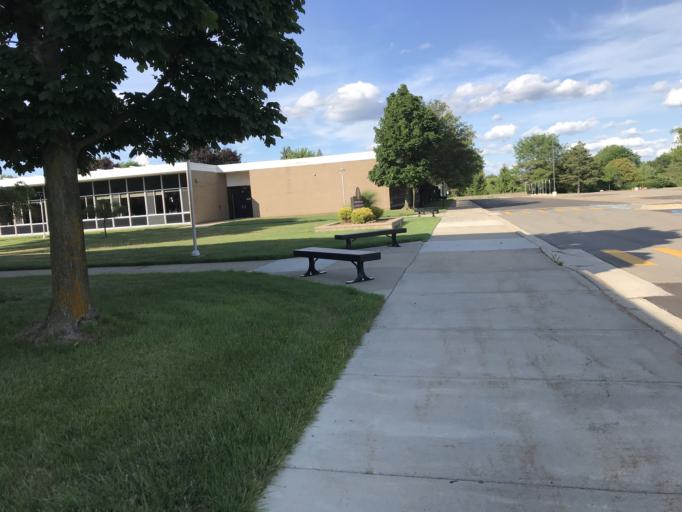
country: US
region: Michigan
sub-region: Oakland County
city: Farmington Hills
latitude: 42.4861
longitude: -83.3366
